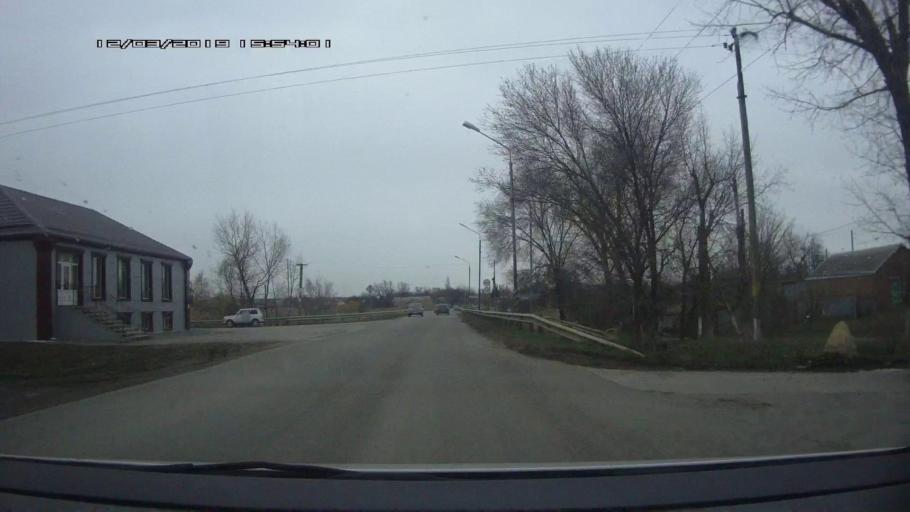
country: RU
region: Rostov
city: Novobataysk
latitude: 46.8882
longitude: 39.7769
